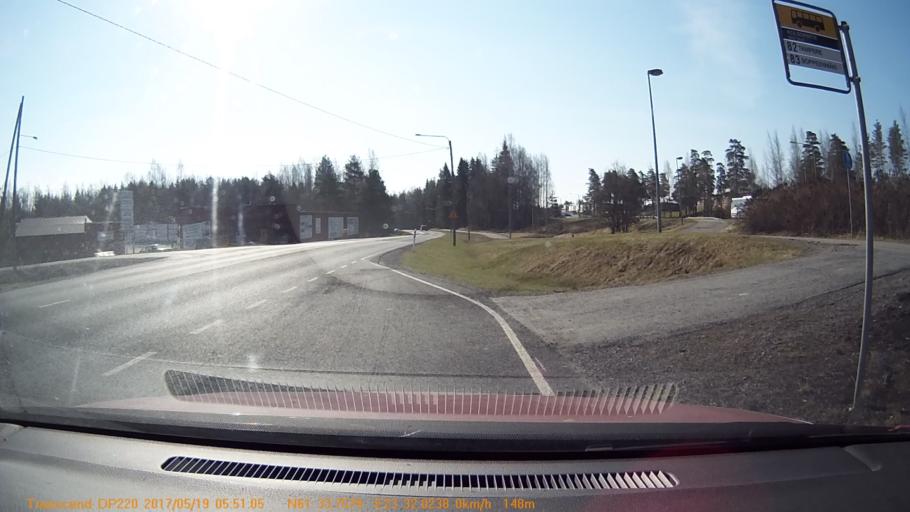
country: FI
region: Pirkanmaa
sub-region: Tampere
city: Yloejaervi
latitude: 61.5626
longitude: 23.5337
